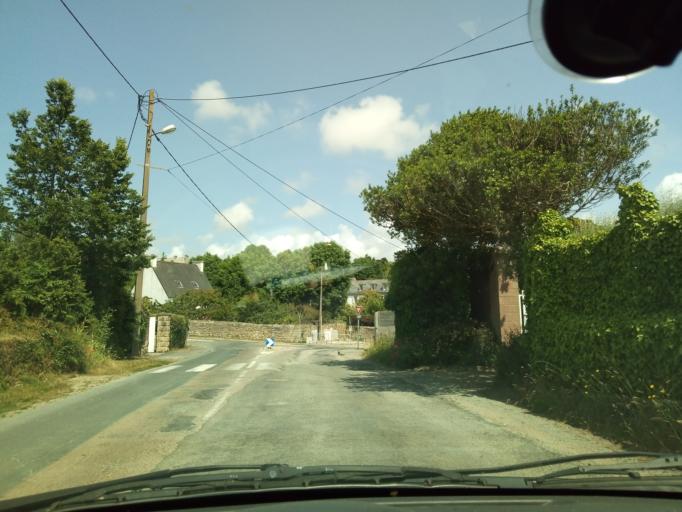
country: FR
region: Brittany
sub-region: Departement du Finistere
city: Esquibien
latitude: 48.0092
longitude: -4.5567
